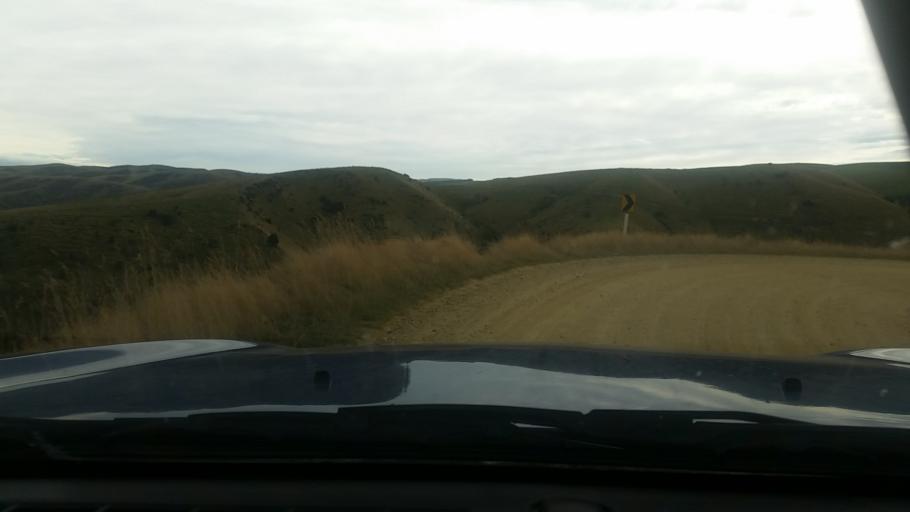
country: NZ
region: Otago
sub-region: Clutha District
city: Balclutha
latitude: -45.7036
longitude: 169.4631
